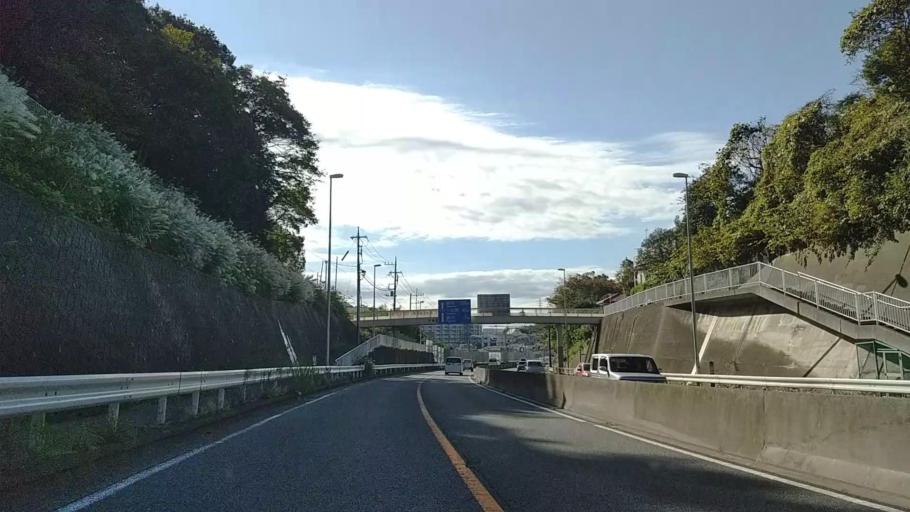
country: JP
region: Kanagawa
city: Fujisawa
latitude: 35.3978
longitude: 139.5280
